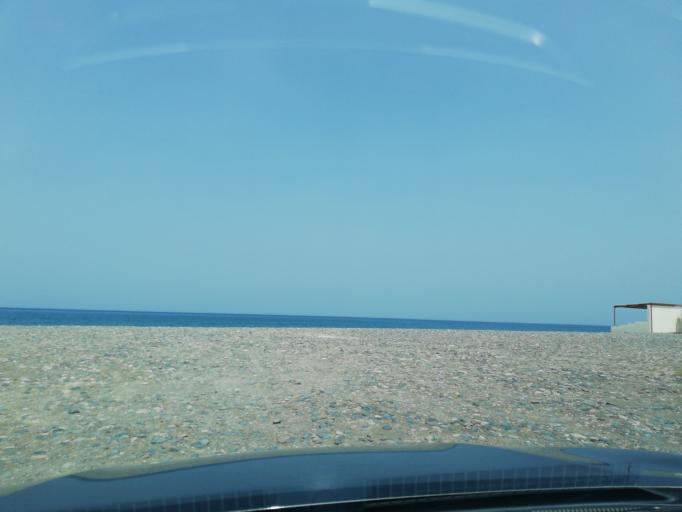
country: OM
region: Al Batinah
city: Shinas
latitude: 24.8652
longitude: 56.4167
